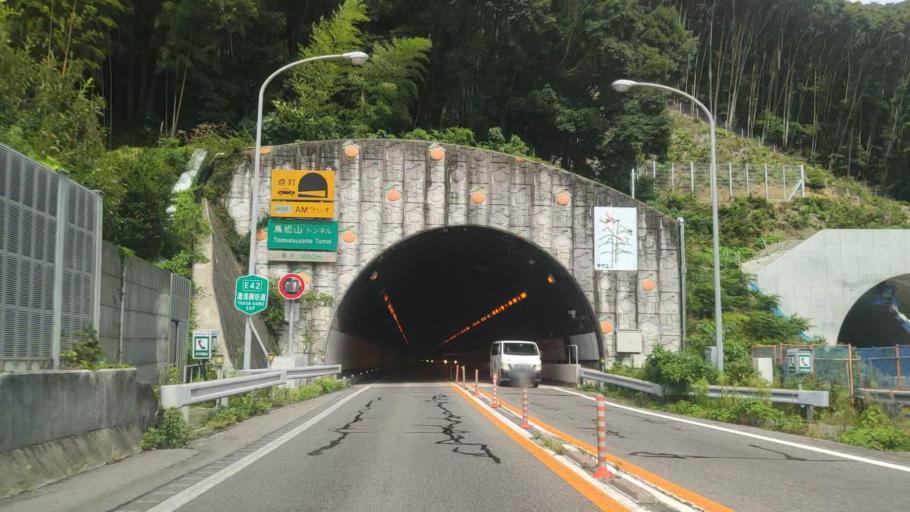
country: JP
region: Wakayama
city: Gobo
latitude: 33.9717
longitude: 135.1975
